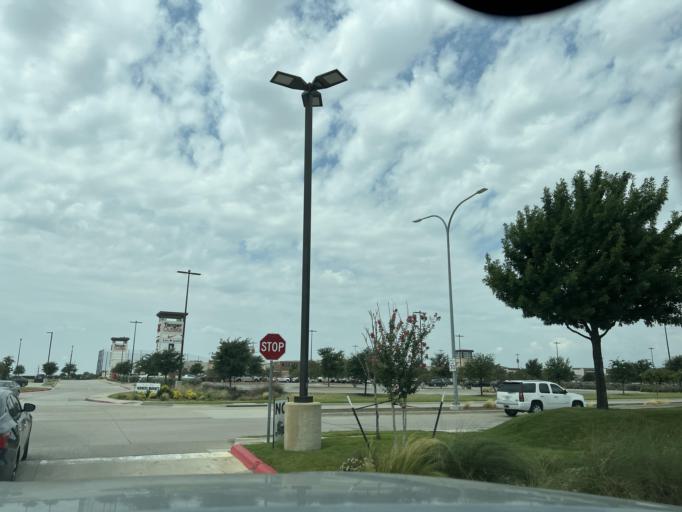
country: US
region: Texas
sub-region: Denton County
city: Roanoke
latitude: 33.0231
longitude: -97.2787
